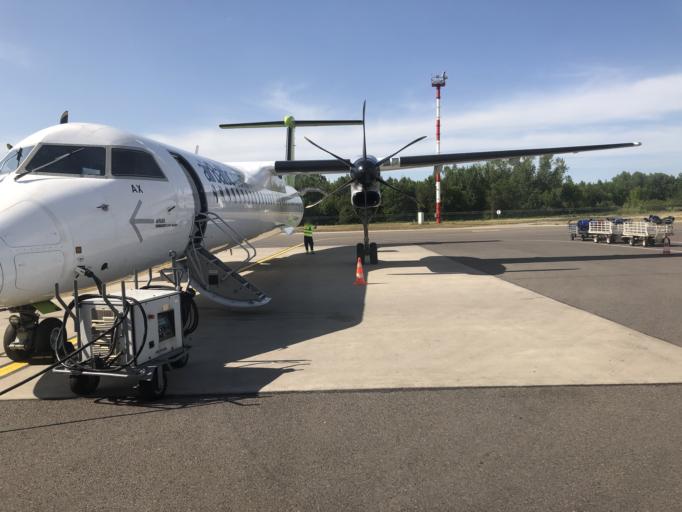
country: LT
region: Vilnius County
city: Naujamiestis
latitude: 54.6451
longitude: 25.2840
